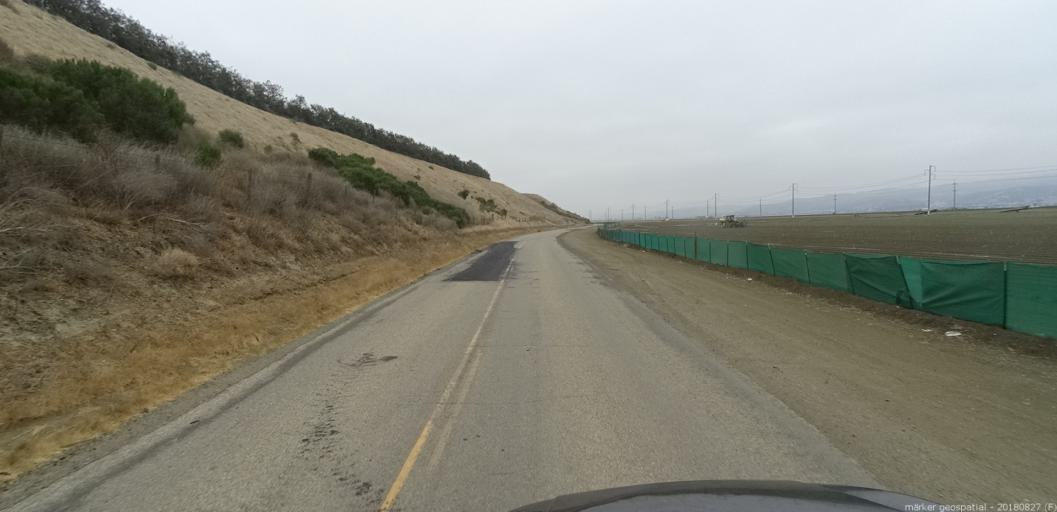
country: US
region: California
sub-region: Monterey County
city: King City
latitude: 36.2501
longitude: -121.1362
